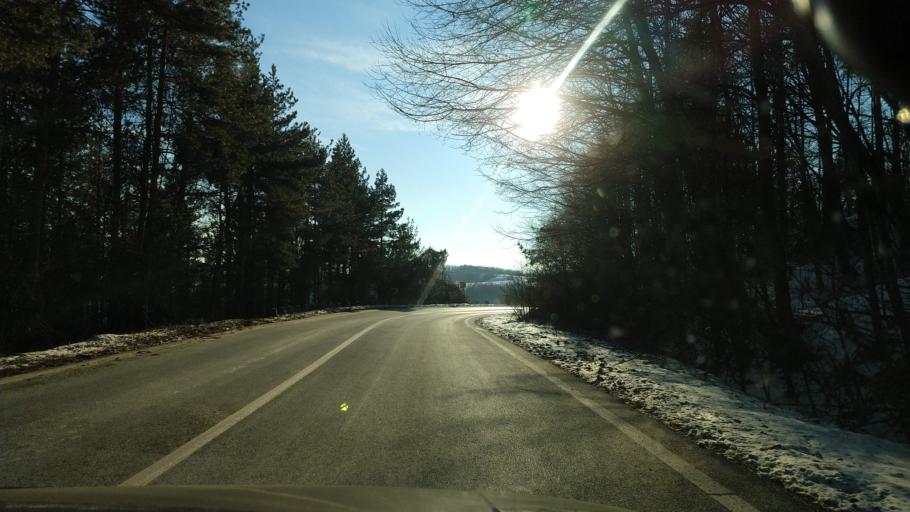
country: RO
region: Bacau
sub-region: Comuna Luizi-Calugara
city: Luizi-Calugara
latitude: 46.4994
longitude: 26.8037
